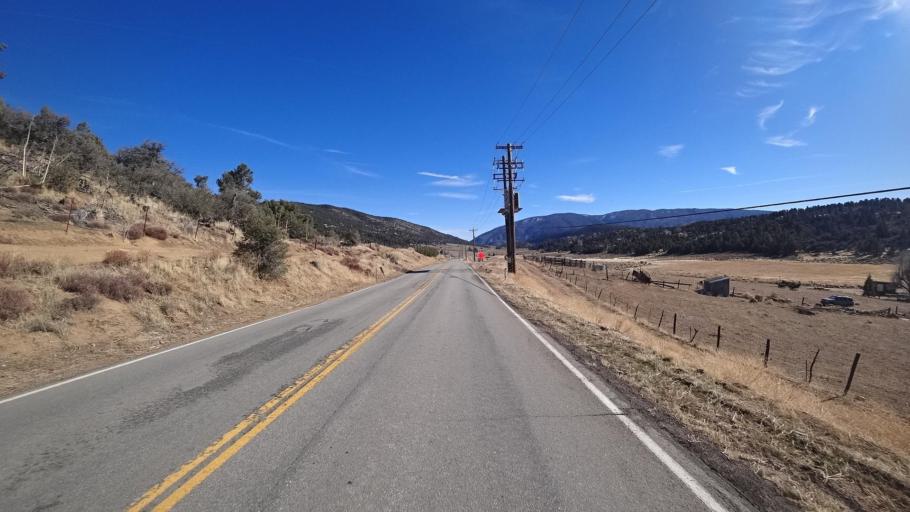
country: US
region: California
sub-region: Kern County
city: Pine Mountain Club
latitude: 34.8389
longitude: -119.0529
